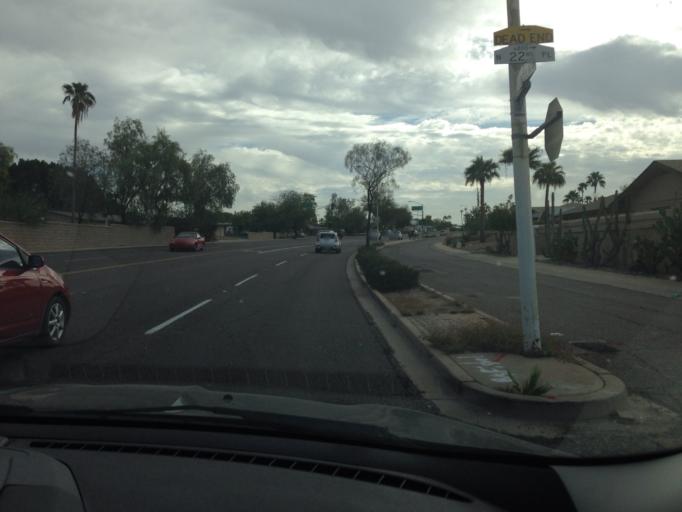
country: US
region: Arizona
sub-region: Maricopa County
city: Paradise Valley
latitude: 33.5376
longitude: -112.0337
